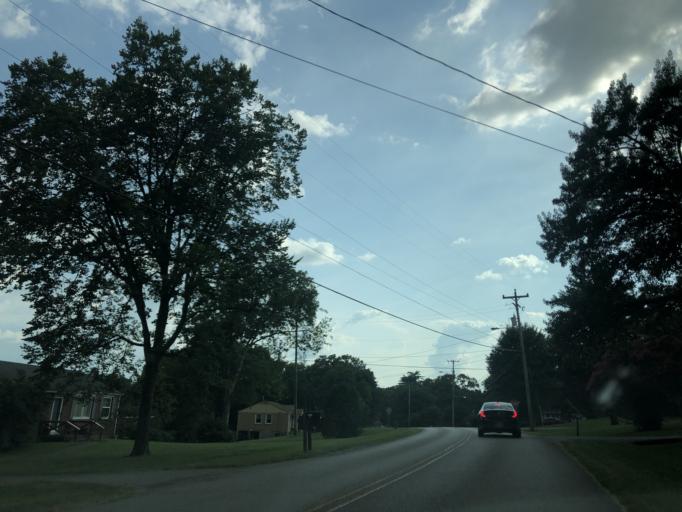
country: US
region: Tennessee
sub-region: Davidson County
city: Lakewood
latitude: 36.1602
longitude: -86.6734
